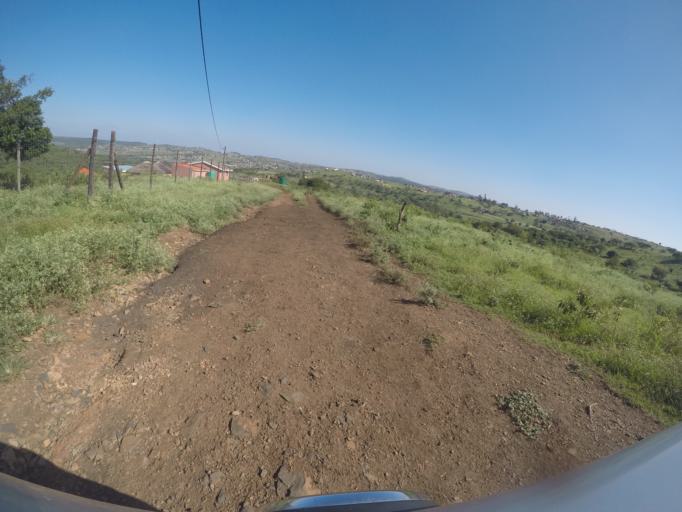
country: ZA
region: KwaZulu-Natal
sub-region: uThungulu District Municipality
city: Empangeni
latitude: -28.5736
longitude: 31.7315
